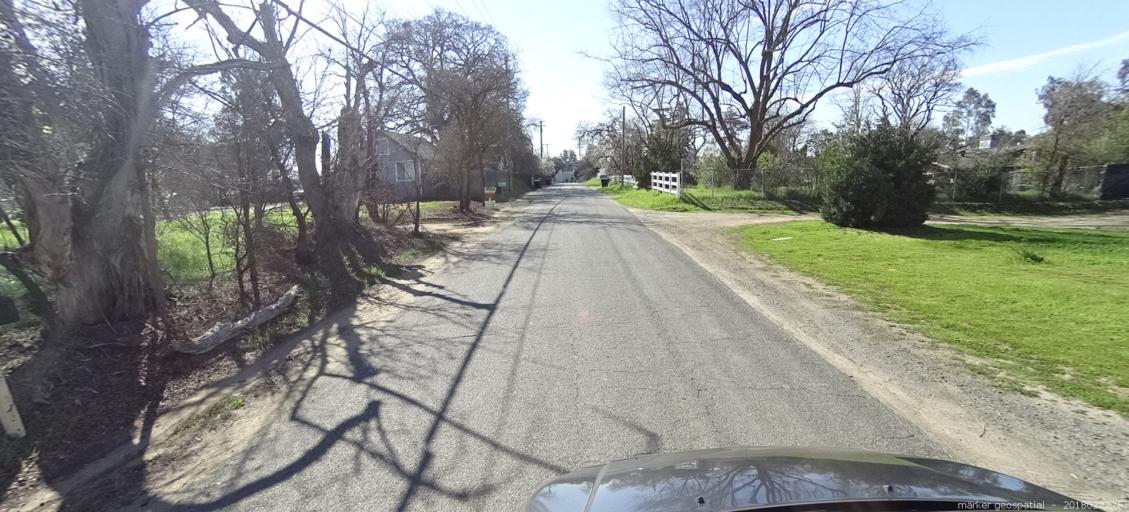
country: US
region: California
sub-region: Sacramento County
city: Rio Linda
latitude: 38.6997
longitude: -121.4337
